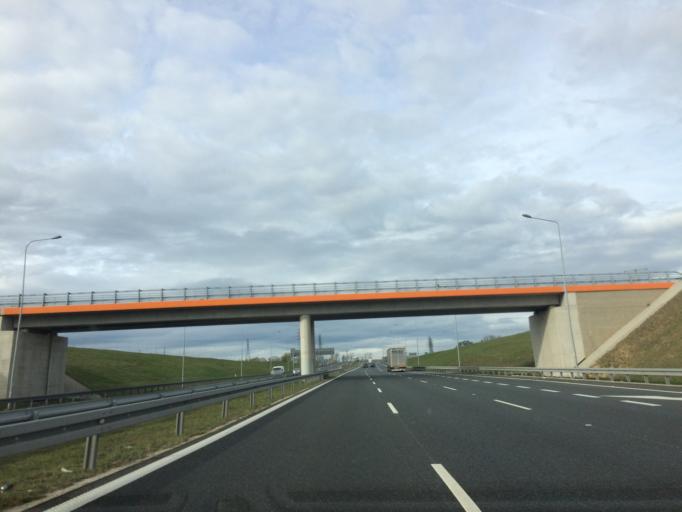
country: PL
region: Lower Silesian Voivodeship
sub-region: Legnica
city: Legnica
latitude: 51.1751
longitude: 16.0925
